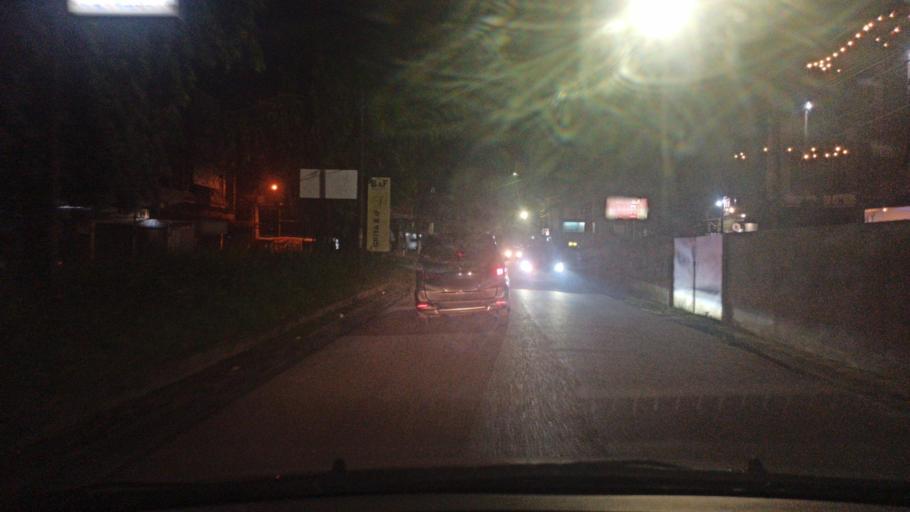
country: ID
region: South Sumatra
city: Palembang
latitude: -2.9289
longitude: 104.7882
